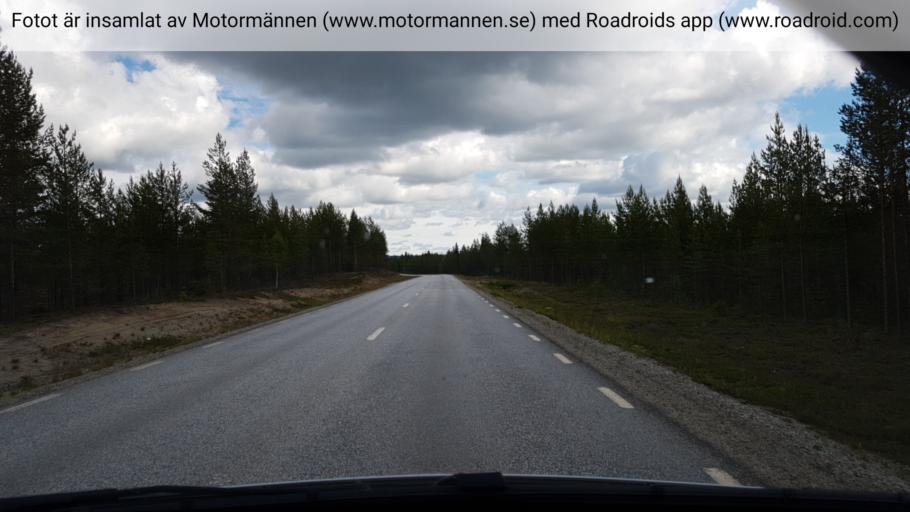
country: SE
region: Vaesterbotten
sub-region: Vindelns Kommun
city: Vindeln
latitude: 64.2101
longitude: 19.4063
